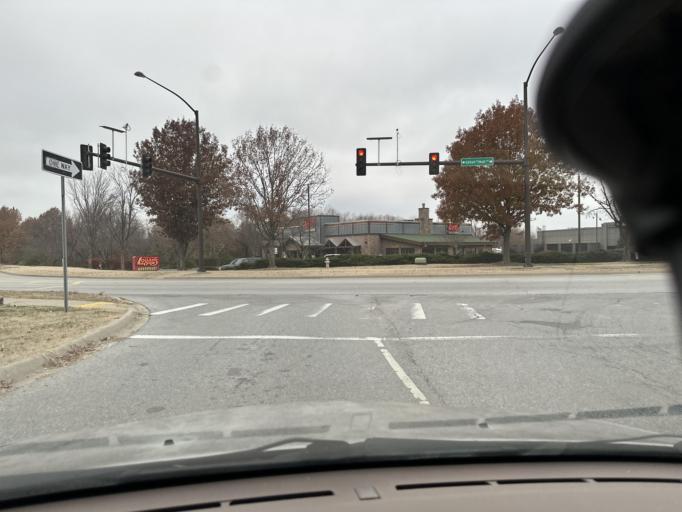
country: US
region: Arkansas
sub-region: Washington County
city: Johnson
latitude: 36.1163
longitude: -94.1501
